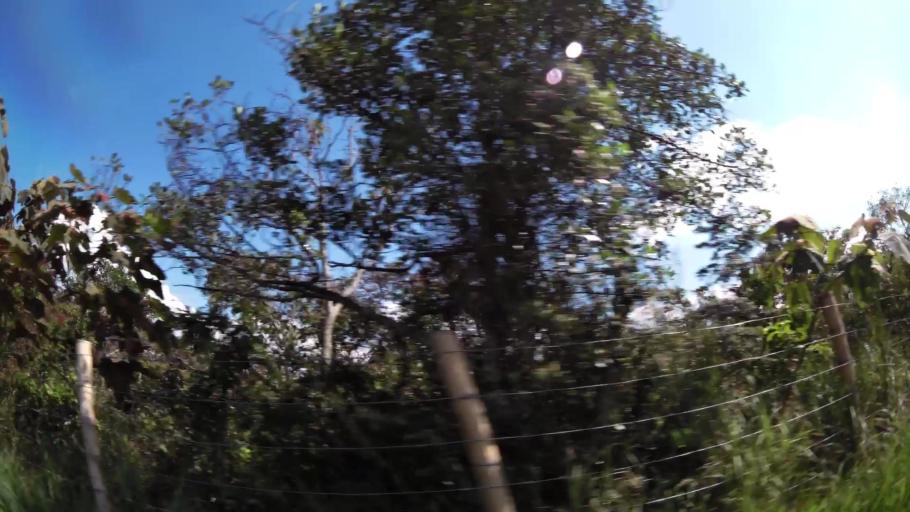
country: CO
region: Valle del Cauca
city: Cali
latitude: 3.4310
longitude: -76.5711
